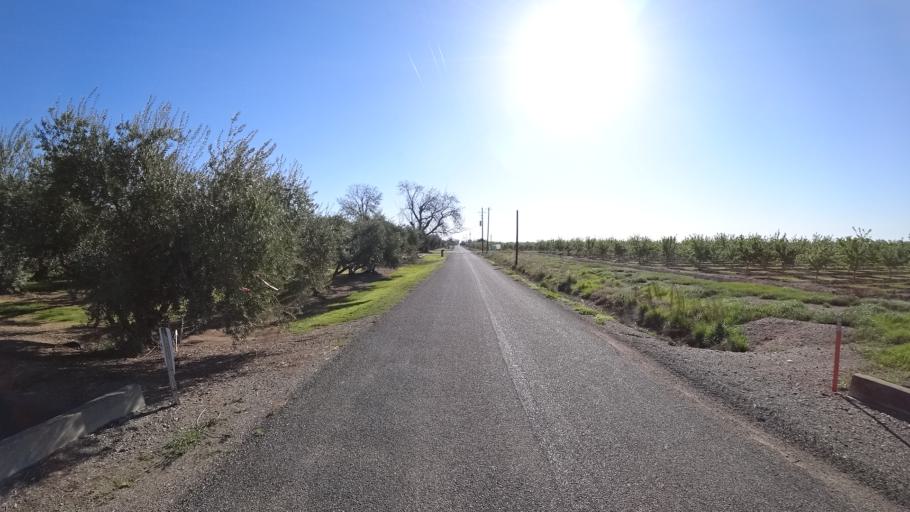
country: US
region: California
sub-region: Glenn County
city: Orland
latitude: 39.7261
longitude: -122.2406
